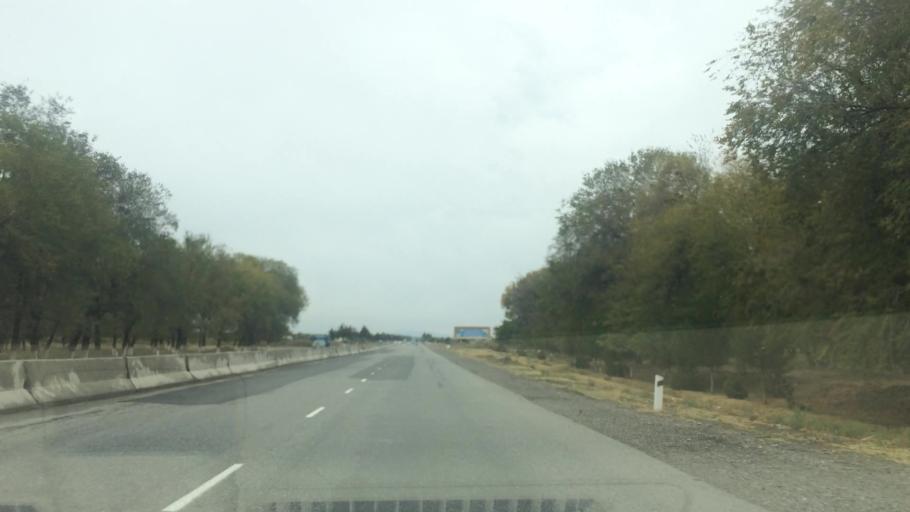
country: UZ
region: Samarqand
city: Bulung'ur
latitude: 39.7943
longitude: 67.3284
